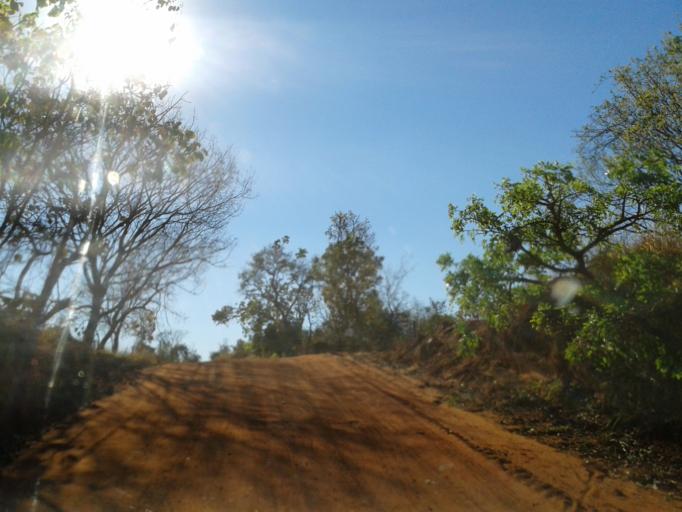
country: BR
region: Minas Gerais
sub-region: Ituiutaba
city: Ituiutaba
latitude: -19.0588
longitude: -49.3585
